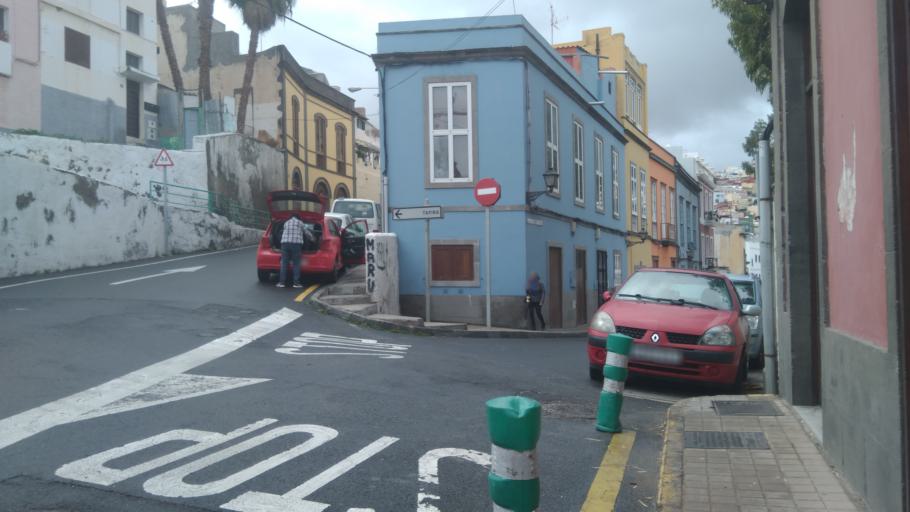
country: ES
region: Canary Islands
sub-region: Provincia de Las Palmas
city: Las Palmas de Gran Canaria
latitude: 28.0988
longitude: -15.4192
